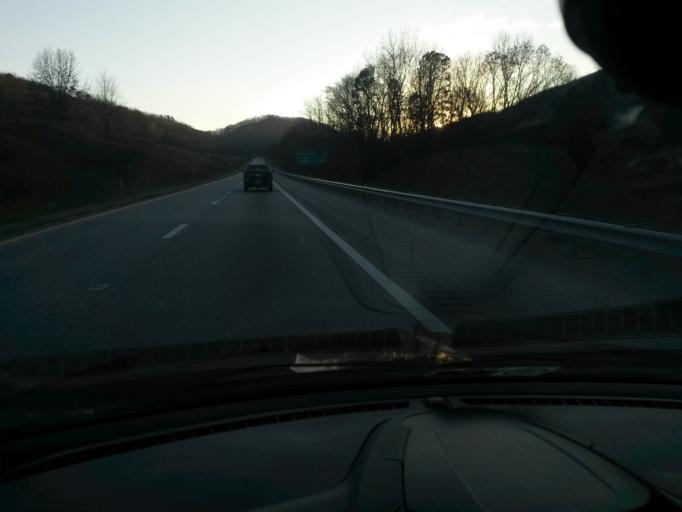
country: US
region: Virginia
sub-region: City of Lexington
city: Lexington
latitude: 37.8814
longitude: -79.6043
